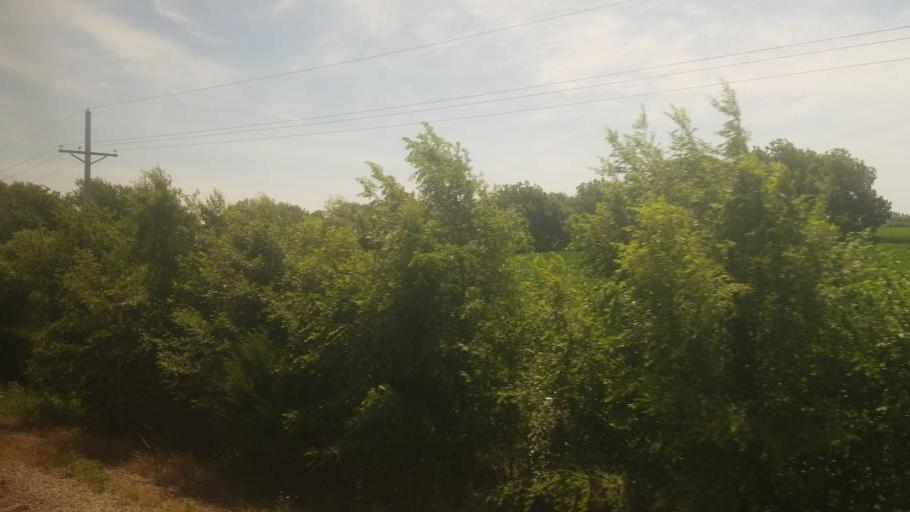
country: US
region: Missouri
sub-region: Carroll County
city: Carrollton
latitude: 39.3017
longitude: -93.6856
